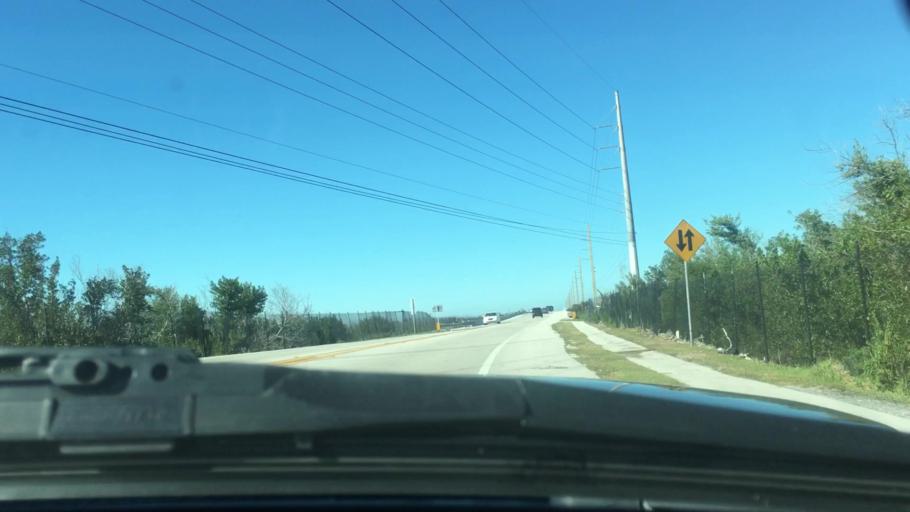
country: US
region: Florida
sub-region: Monroe County
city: Big Pine Key
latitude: 24.6509
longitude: -81.3340
